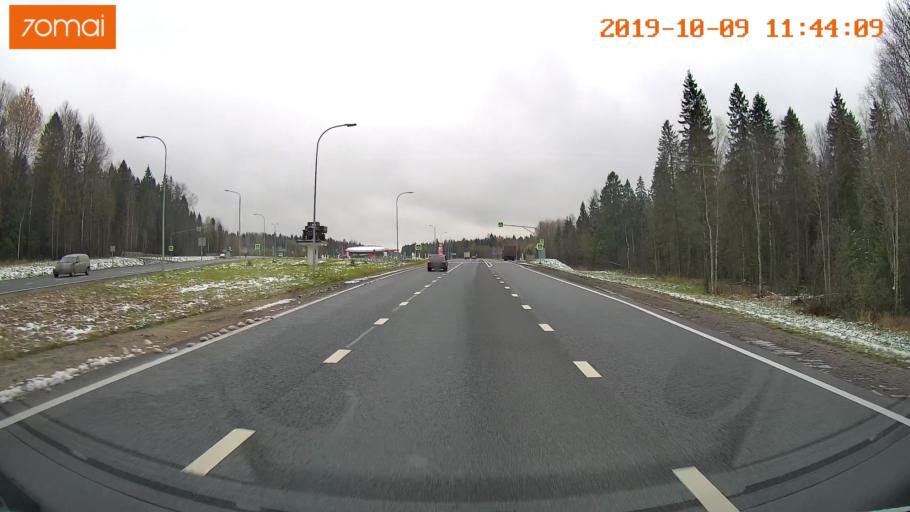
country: RU
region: Vologda
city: Gryazovets
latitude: 58.8870
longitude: 40.1898
